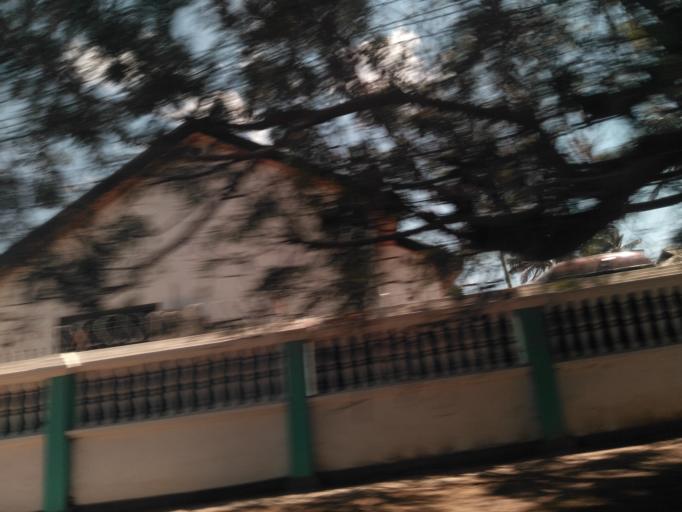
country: TZ
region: Dodoma
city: Dodoma
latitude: -6.1618
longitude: 35.7547
